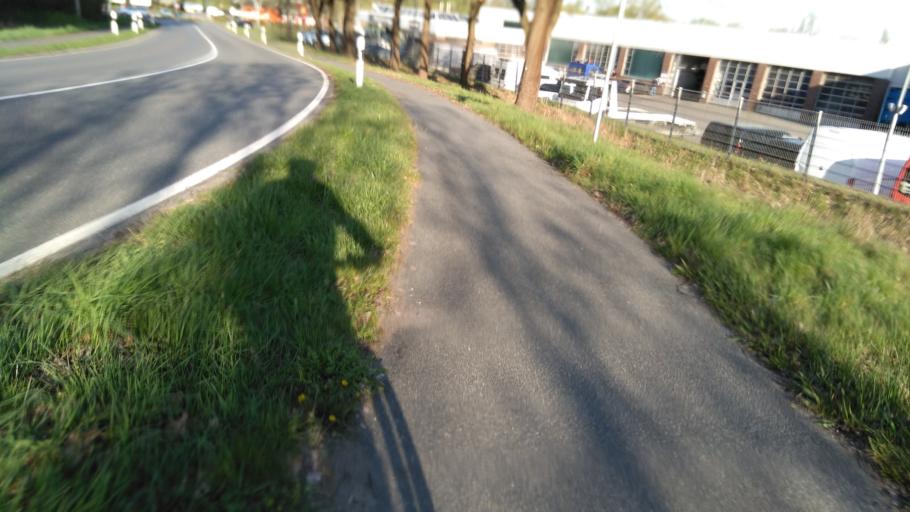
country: DE
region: Lower Saxony
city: Buxtehude
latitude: 53.4616
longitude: 9.6981
